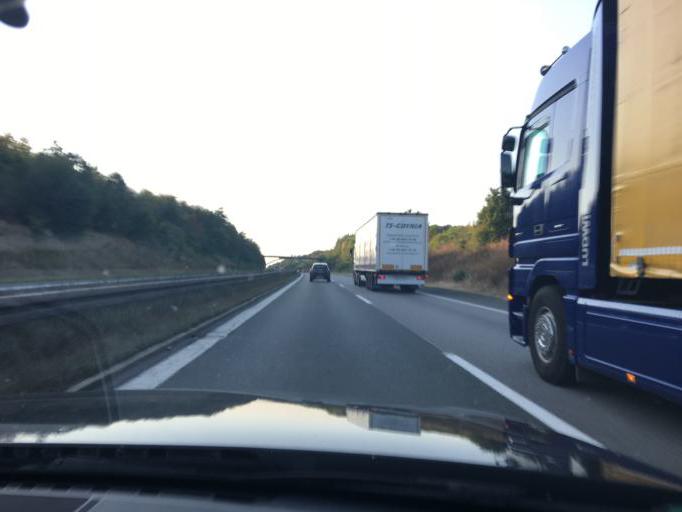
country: DE
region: Bavaria
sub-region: Upper Franconia
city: Strullendorf
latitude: 49.8450
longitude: 10.9968
